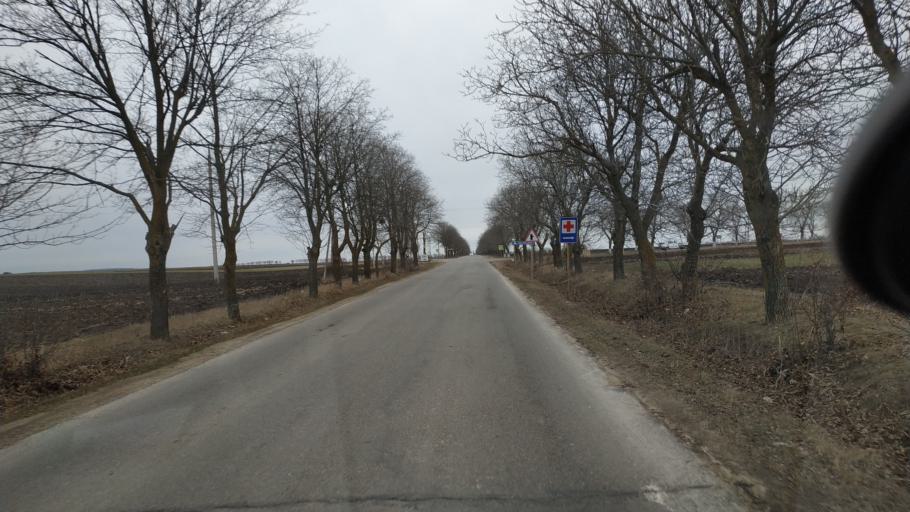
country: MD
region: Telenesti
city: Cocieri
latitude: 47.3093
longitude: 29.0580
